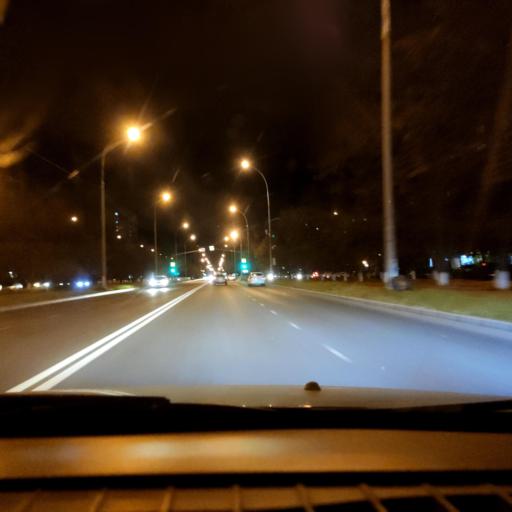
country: RU
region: Samara
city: Tol'yatti
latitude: 53.5205
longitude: 49.3104
